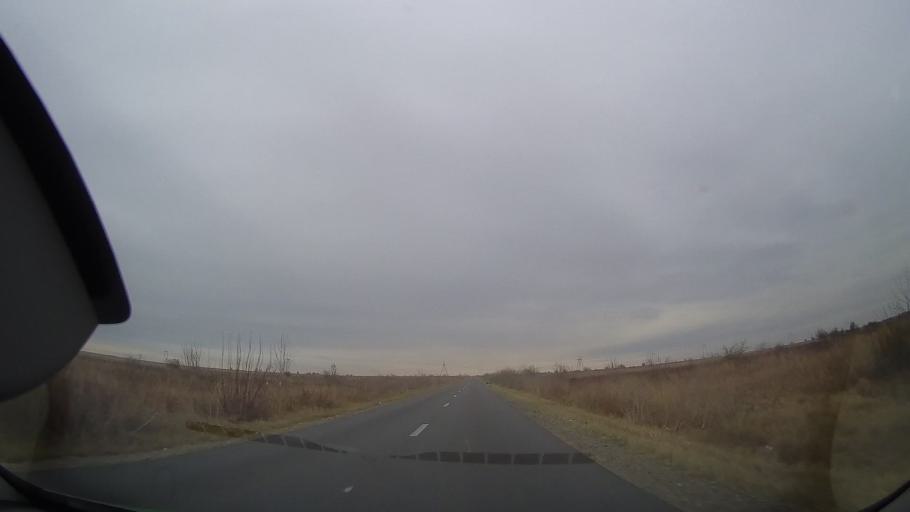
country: RO
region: Ialomita
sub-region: Oras Amara
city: Amara
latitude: 44.6321
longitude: 27.3010
